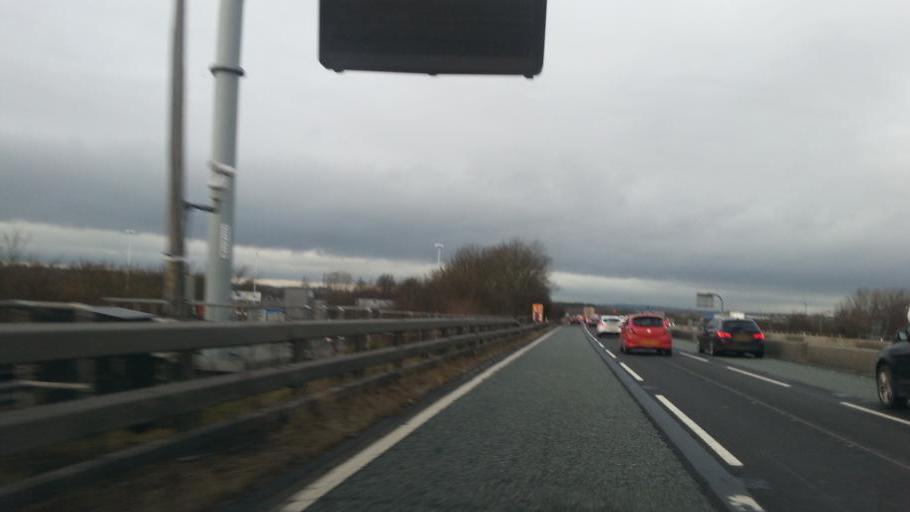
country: GB
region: England
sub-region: City and Borough of Wakefield
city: Normanton
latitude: 53.7084
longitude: -1.3938
